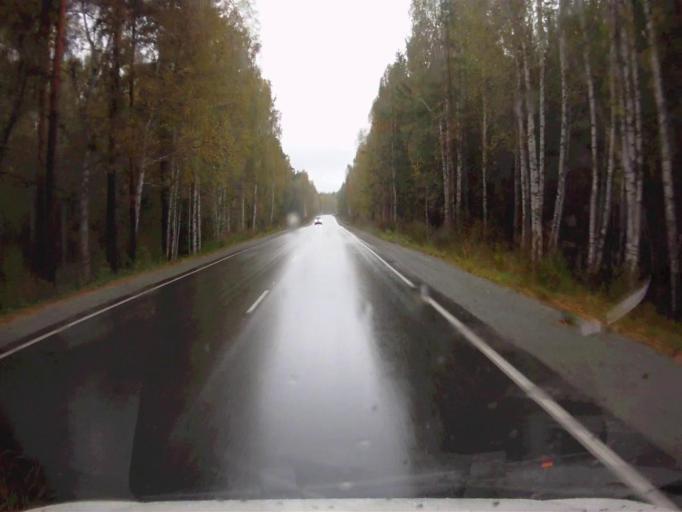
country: RU
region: Chelyabinsk
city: Kyshtym
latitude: 55.6498
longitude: 60.5808
